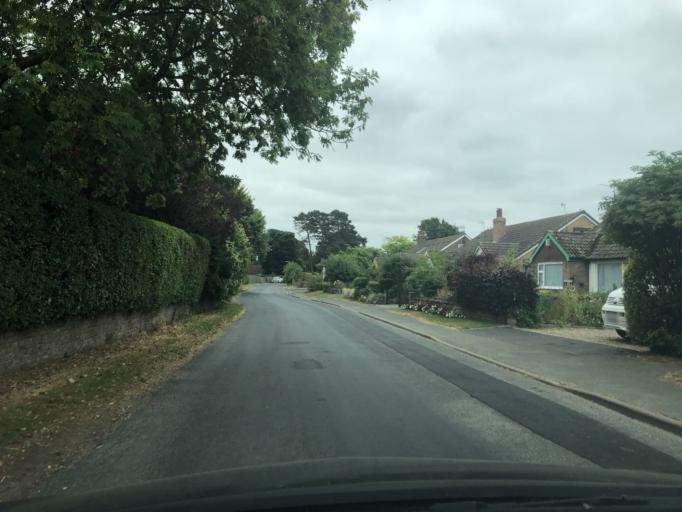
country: GB
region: England
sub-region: North Yorkshire
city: East Ayton
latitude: 54.2452
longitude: -0.4872
